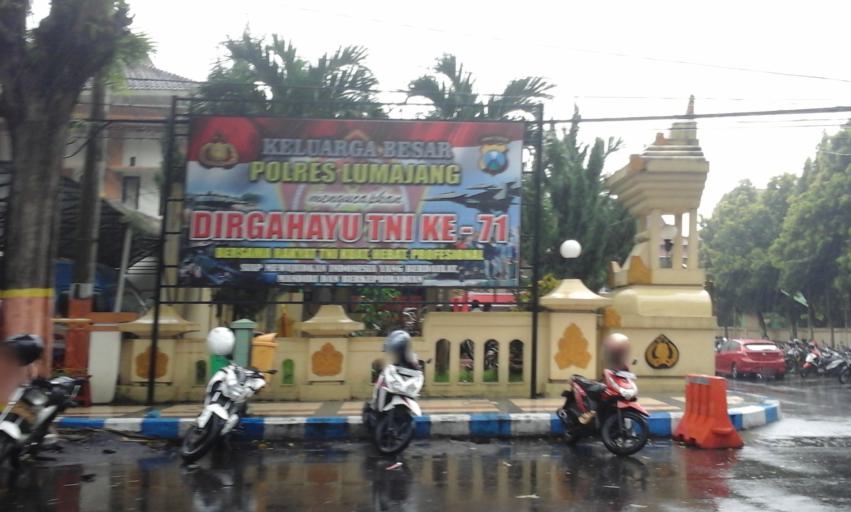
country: ID
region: East Java
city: Lumajang
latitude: -8.1342
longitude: 113.2238
